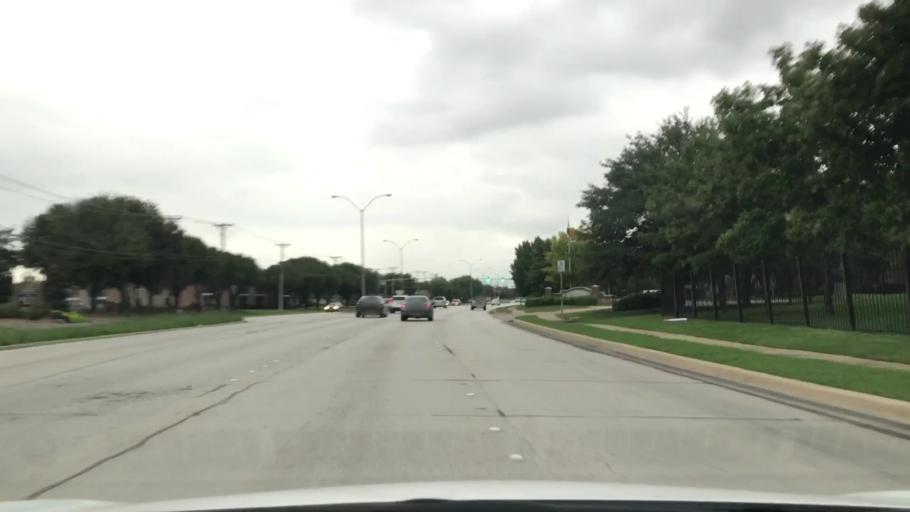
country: US
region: Texas
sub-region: Tarrant County
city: Watauga
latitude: 32.8650
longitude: -97.2911
